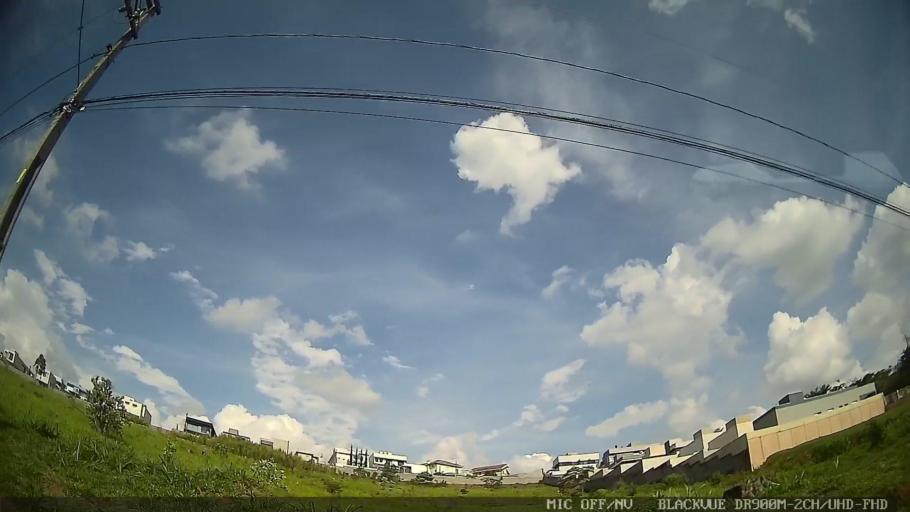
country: BR
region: Sao Paulo
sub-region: Braganca Paulista
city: Braganca Paulista
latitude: -22.9995
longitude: -46.5271
